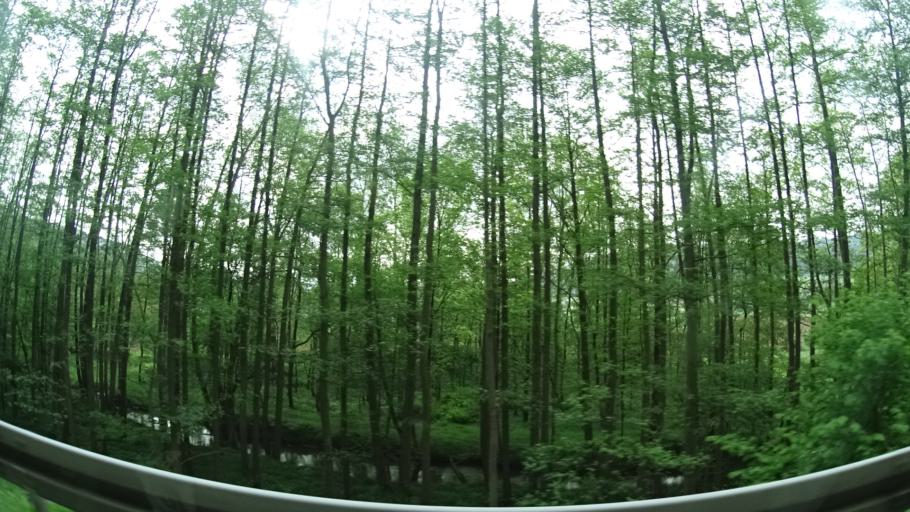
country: DE
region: Bavaria
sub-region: Regierungsbezirk Unterfranken
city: Eschau
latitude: 49.8380
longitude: 9.2711
